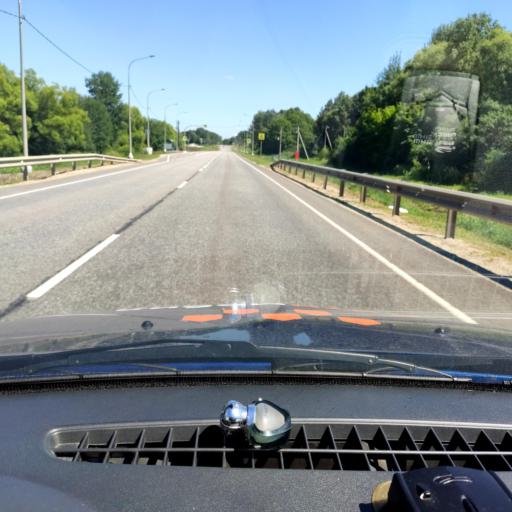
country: RU
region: Orjol
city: Pokrovskoye
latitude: 52.6208
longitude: 36.7320
